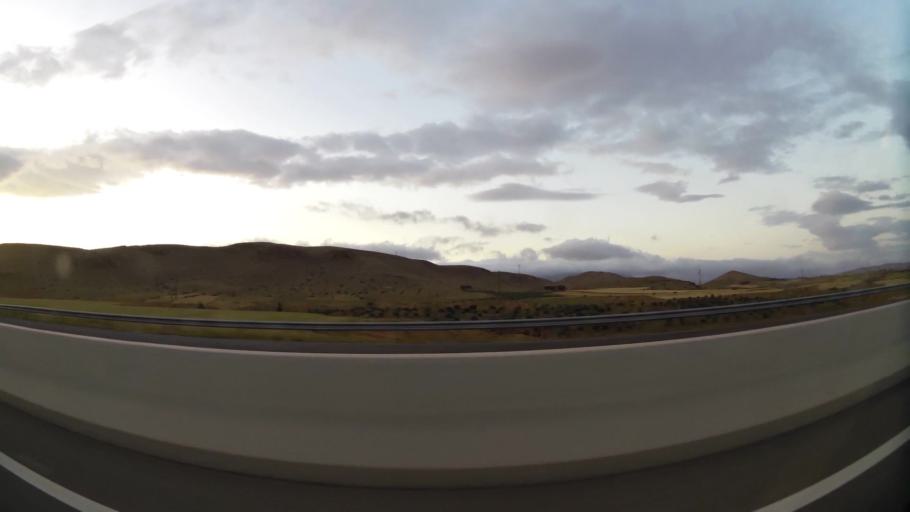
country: MA
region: Oriental
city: El Aioun
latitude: 34.6085
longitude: -2.5696
